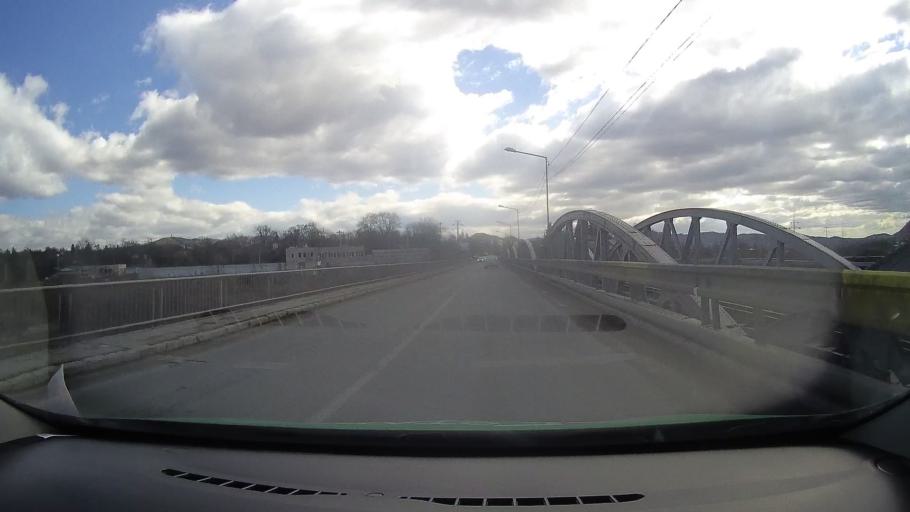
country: RO
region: Dambovita
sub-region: Oras Pucioasa
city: Pucioasa
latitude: 45.0819
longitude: 25.4244
